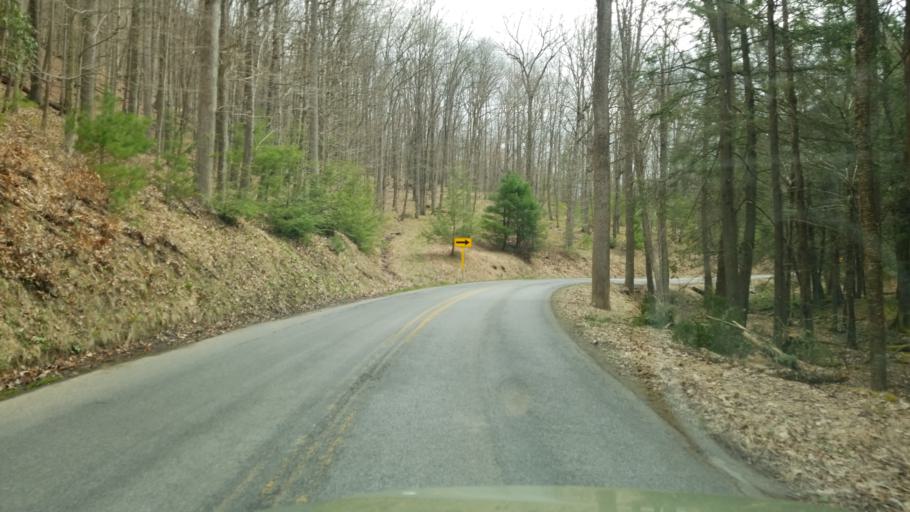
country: US
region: Pennsylvania
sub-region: Cameron County
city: Emporium
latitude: 41.2949
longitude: -78.1153
